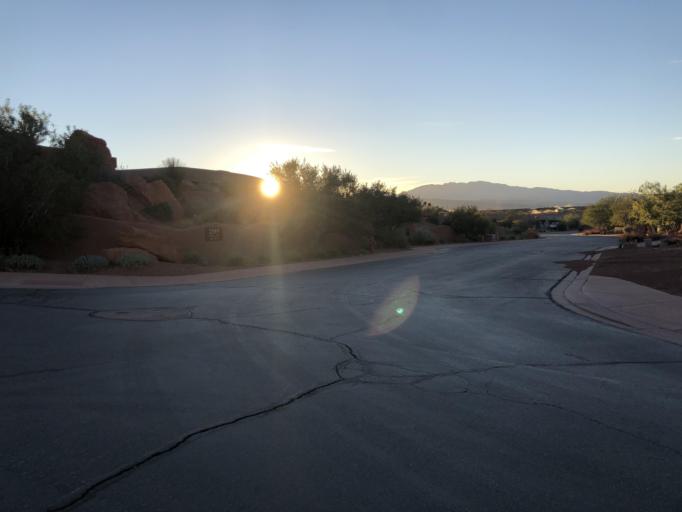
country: US
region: Utah
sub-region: Washington County
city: Santa Clara
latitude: 37.1553
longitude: -113.6385
